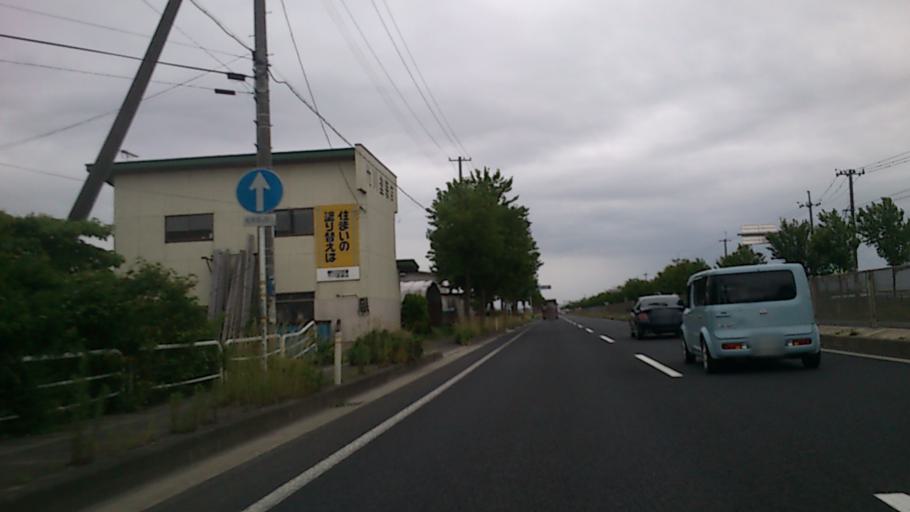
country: JP
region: Yamagata
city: Higashine
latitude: 38.4732
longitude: 140.3829
